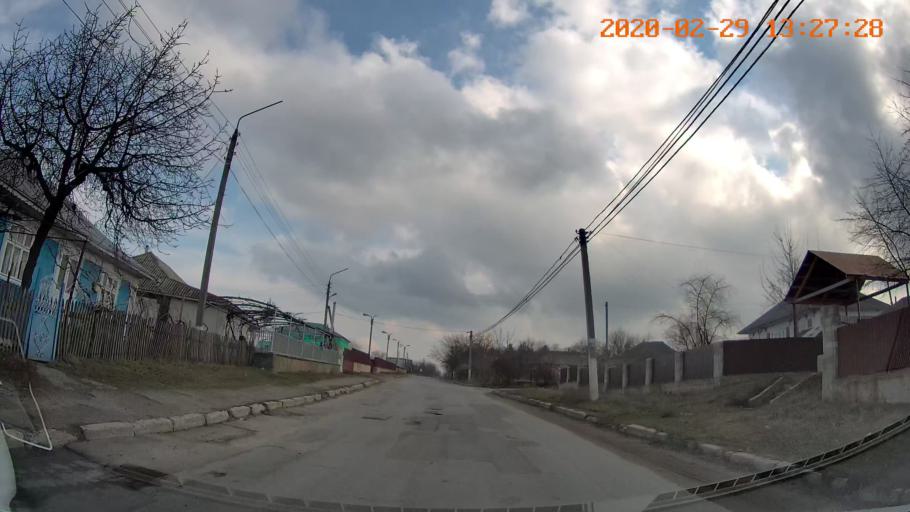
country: MD
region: Telenesti
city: Camenca
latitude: 47.9117
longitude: 28.6418
